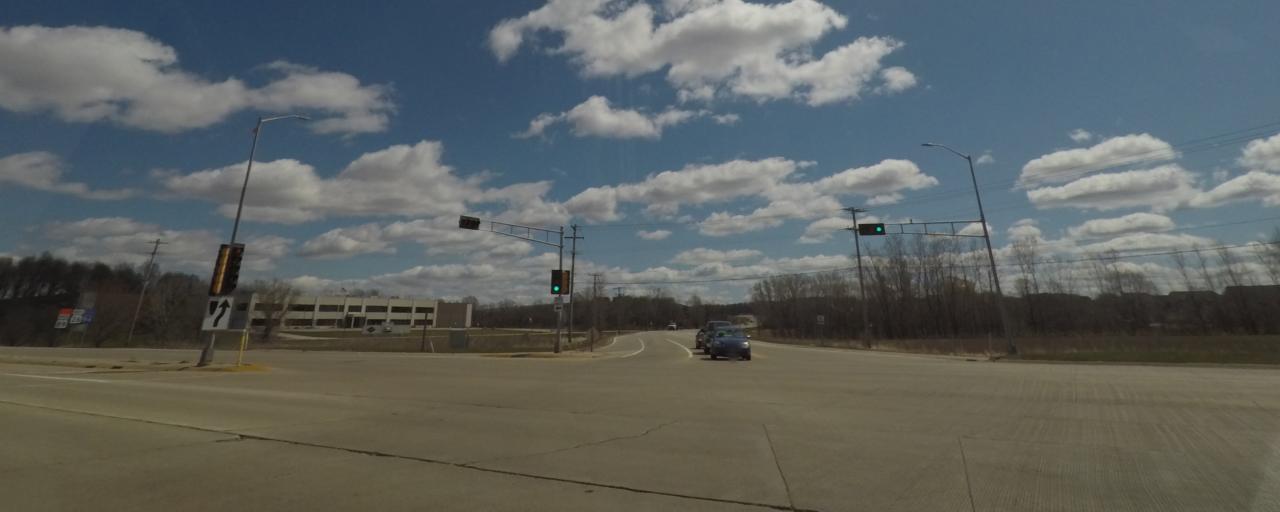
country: US
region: Wisconsin
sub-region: Jefferson County
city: Johnson Creek
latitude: 43.0753
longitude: -88.7679
